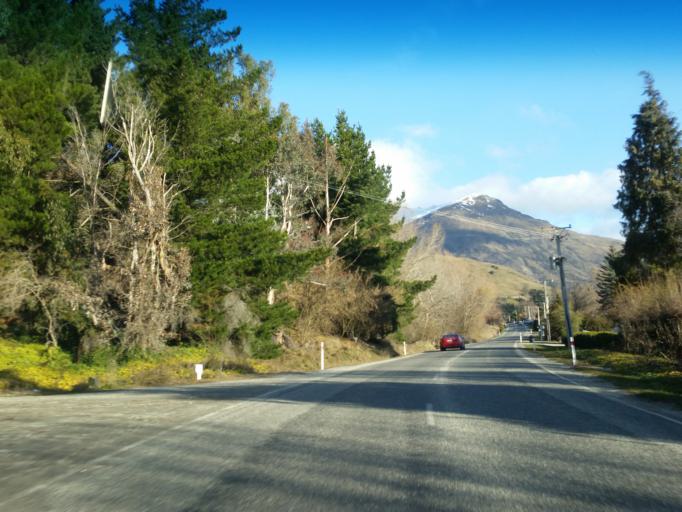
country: NZ
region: Otago
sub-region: Queenstown-Lakes District
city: Arrowtown
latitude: -44.9806
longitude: 168.8177
